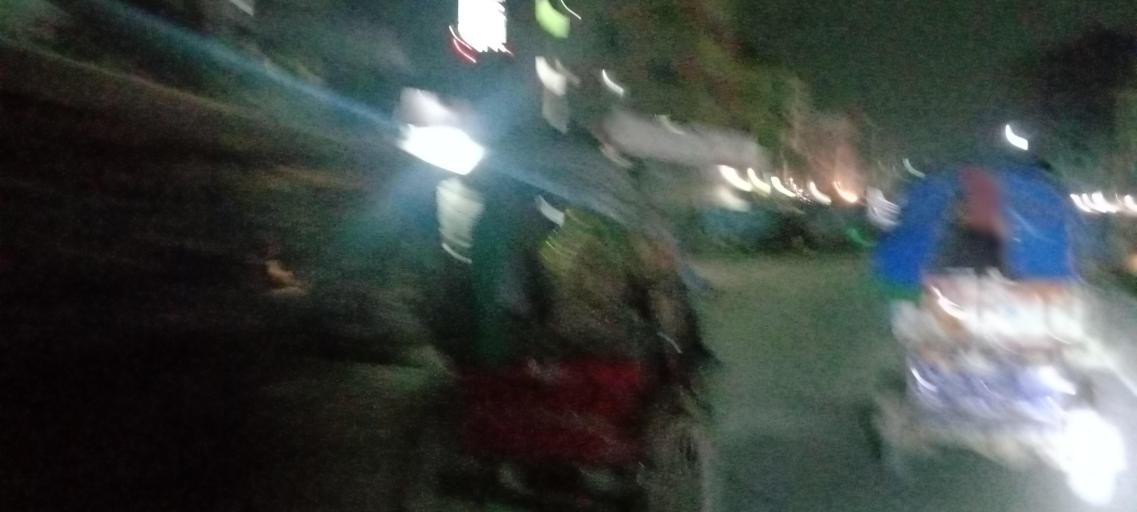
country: BD
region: Dhaka
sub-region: Dhaka
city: Dhaka
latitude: 23.7018
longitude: 90.3915
